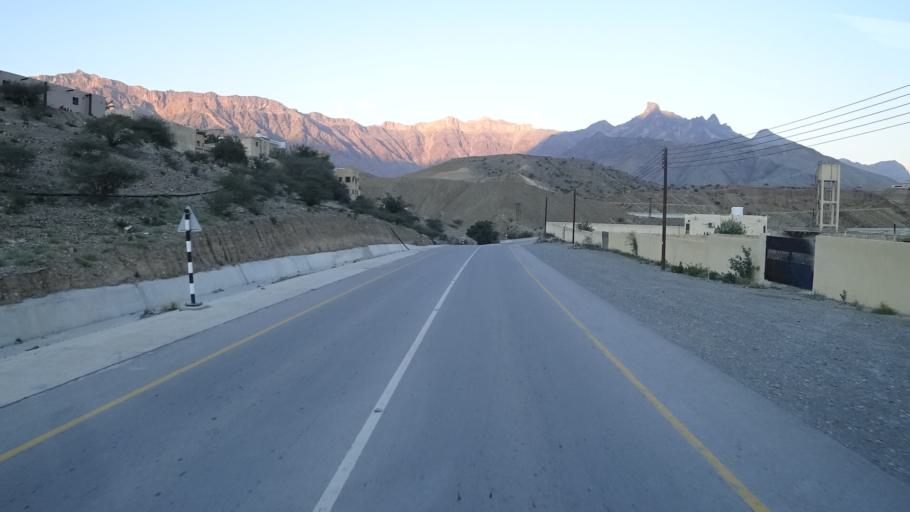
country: OM
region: Al Batinah
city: Rustaq
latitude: 23.2849
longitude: 57.3309
